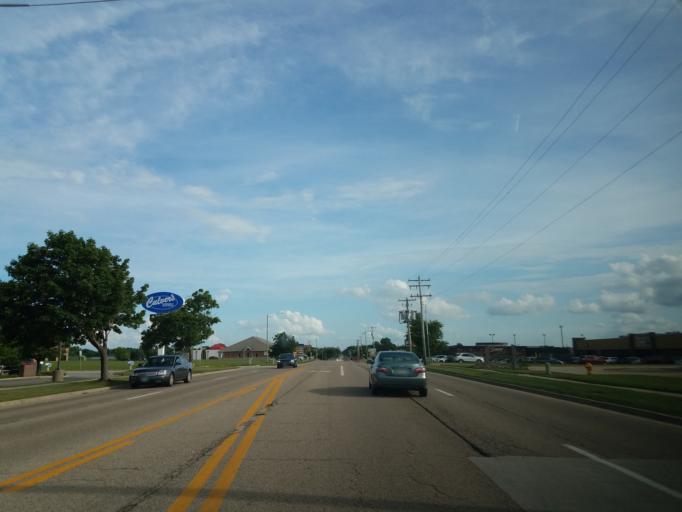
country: US
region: Illinois
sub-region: McLean County
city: Bloomington
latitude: 40.4868
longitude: -88.9433
